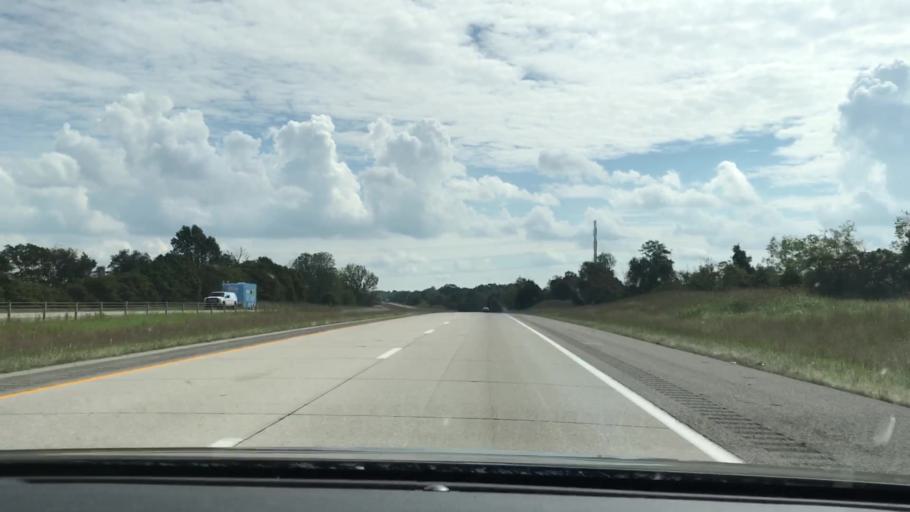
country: US
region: Kentucky
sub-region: Trigg County
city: Cadiz
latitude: 36.9017
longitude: -87.7680
